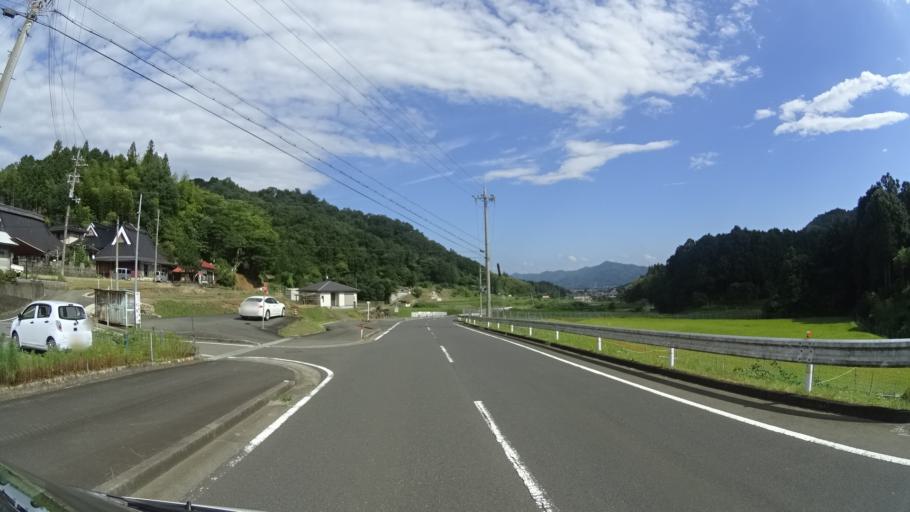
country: JP
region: Kyoto
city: Fukuchiyama
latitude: 35.3402
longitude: 135.1670
